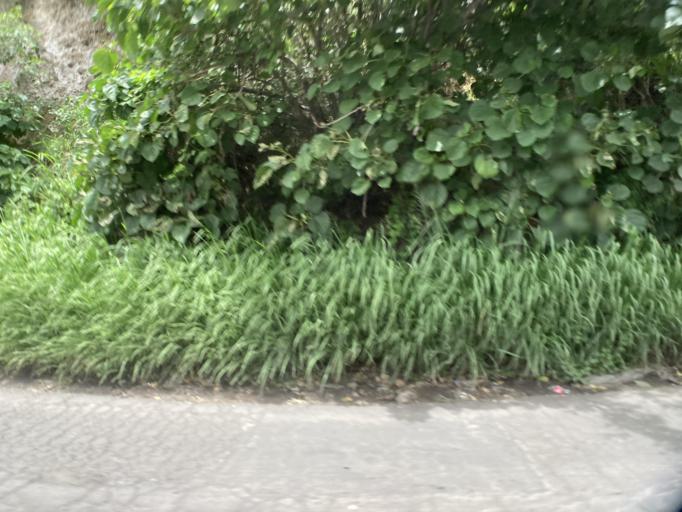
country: GT
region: Guatemala
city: Villa Canales
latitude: 14.4569
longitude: -90.5744
